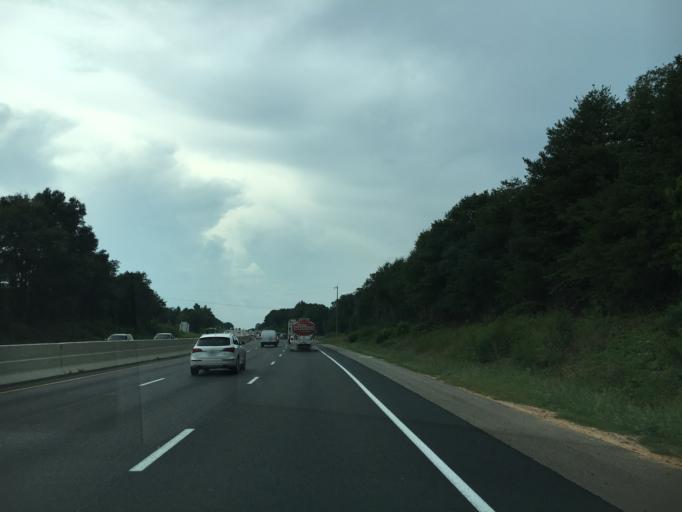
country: US
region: South Carolina
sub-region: Spartanburg County
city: Wellford
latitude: 34.9504
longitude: -82.0688
